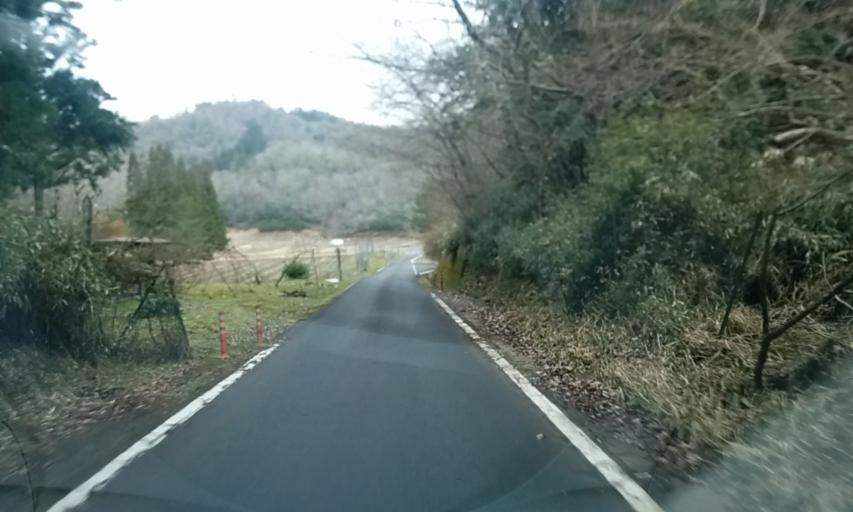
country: JP
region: Kyoto
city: Kameoka
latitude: 35.1144
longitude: 135.4259
